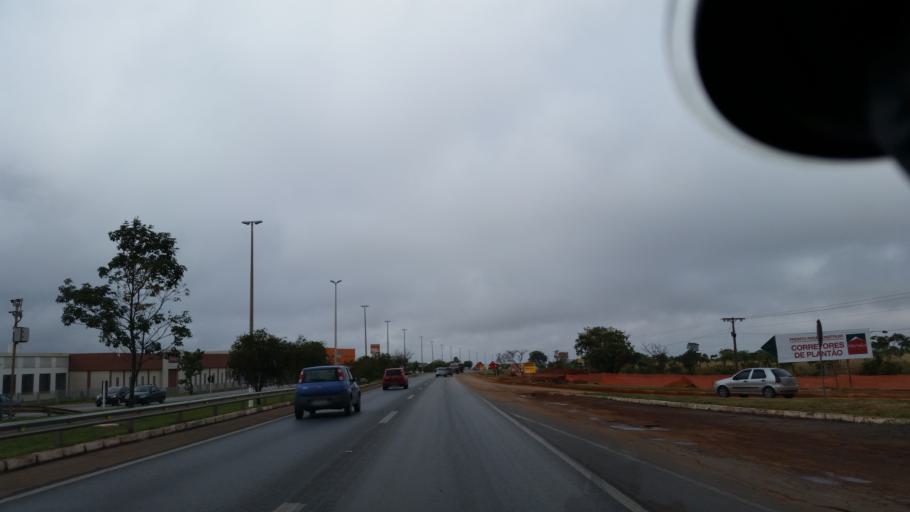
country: BR
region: Goias
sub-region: Luziania
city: Luziania
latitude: -16.0267
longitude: -47.9794
